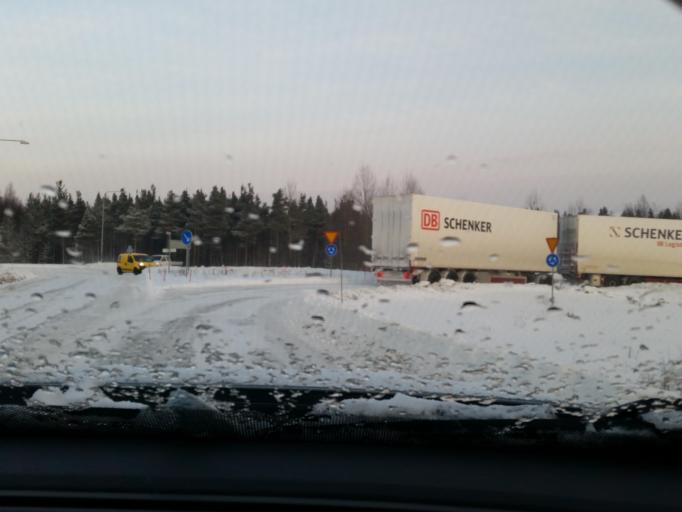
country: SE
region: Norrbotten
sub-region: Pitea Kommun
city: Bergsviken
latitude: 65.3213
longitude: 21.4201
